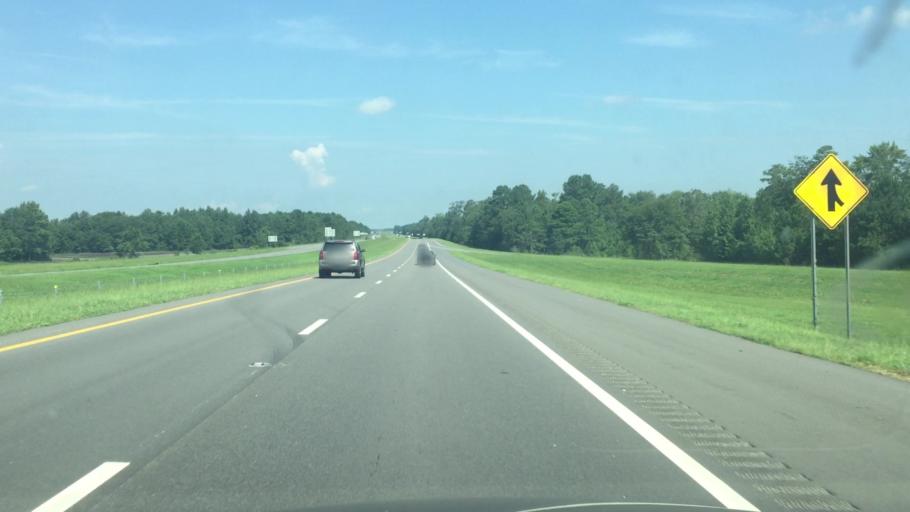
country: US
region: North Carolina
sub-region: Robeson County
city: Pembroke
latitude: 34.6527
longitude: -79.2465
